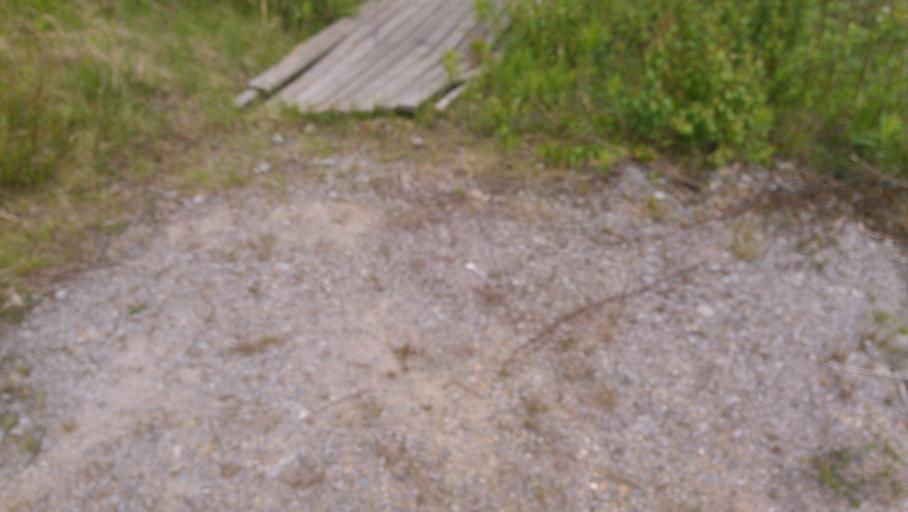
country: SE
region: Vaesterbotten
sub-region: Umea Kommun
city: Roback
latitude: 63.8856
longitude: 20.0367
